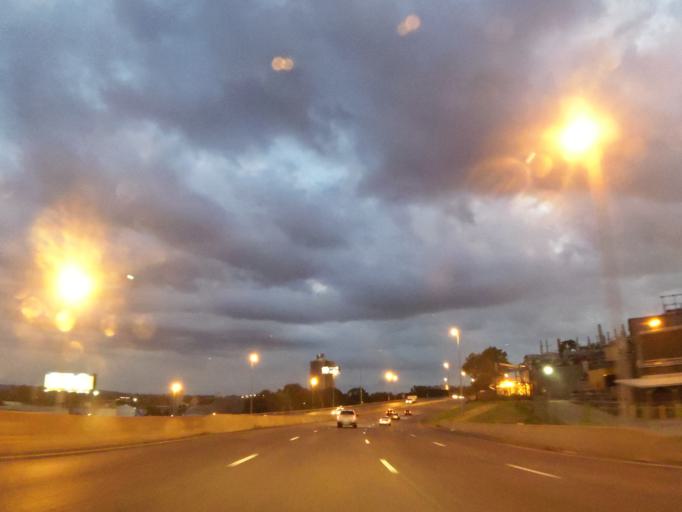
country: US
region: Illinois
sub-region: Saint Clair County
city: Cahokia
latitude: 38.5884
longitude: -90.2144
